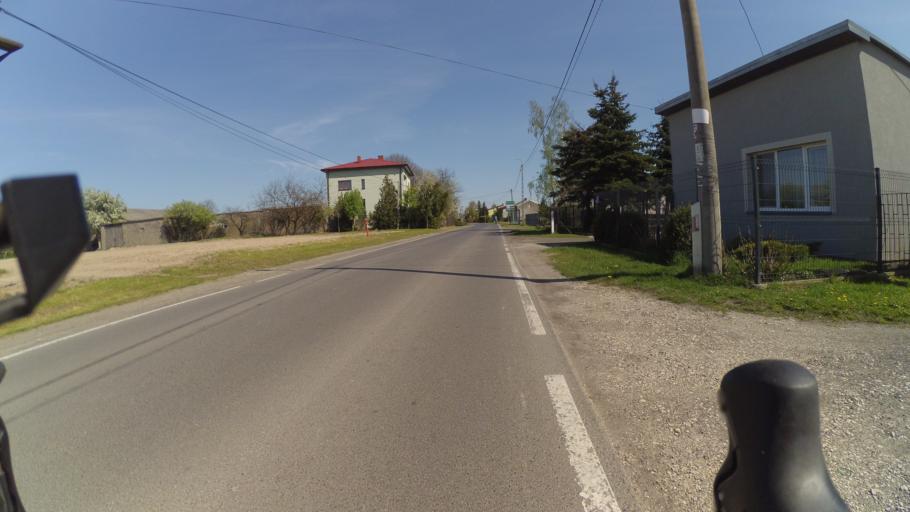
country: PL
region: Masovian Voivodeship
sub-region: Powiat warszawski zachodni
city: Leszno
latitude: 52.2446
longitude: 20.5454
